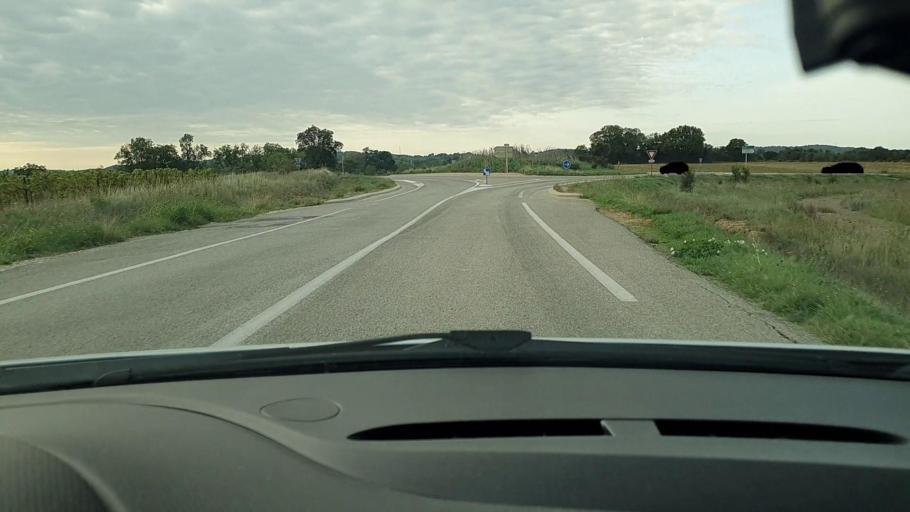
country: FR
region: Languedoc-Roussillon
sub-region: Departement du Gard
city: Mons
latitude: 44.0767
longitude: 4.2196
